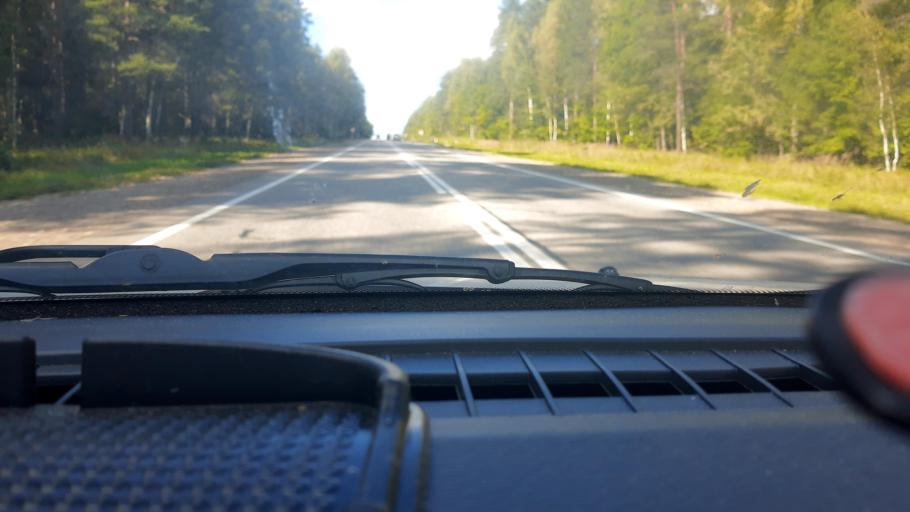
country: RU
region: Nizjnij Novgorod
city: Surovatikha
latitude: 55.7273
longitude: 43.9887
